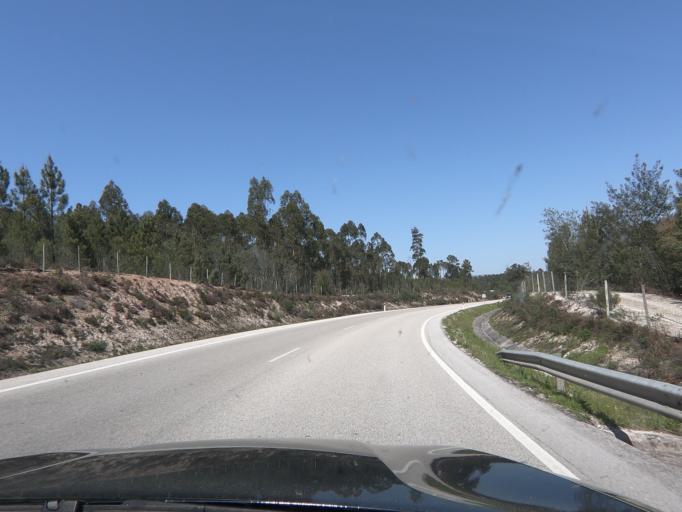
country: PT
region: Coimbra
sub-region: Lousa
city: Lousa
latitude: 40.1230
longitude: -8.2814
